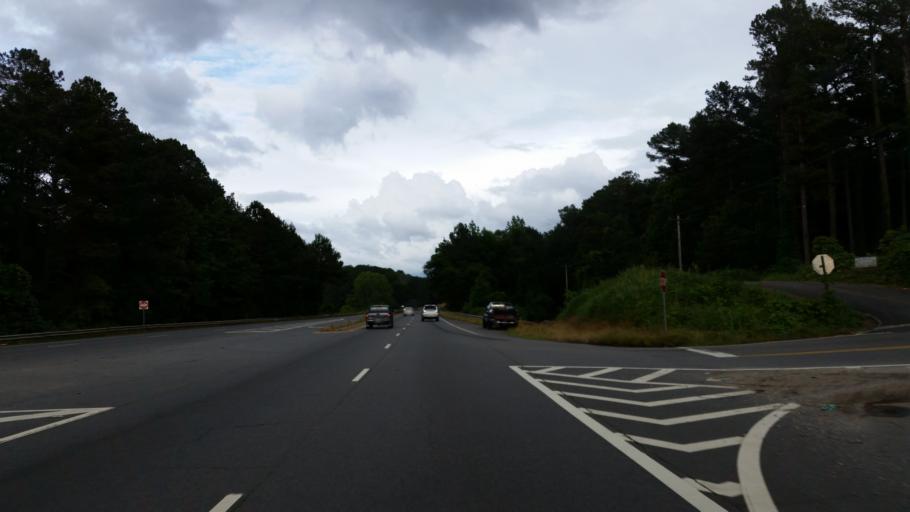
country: US
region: Georgia
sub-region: Cobb County
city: Acworth
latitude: 34.0569
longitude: -84.7134
